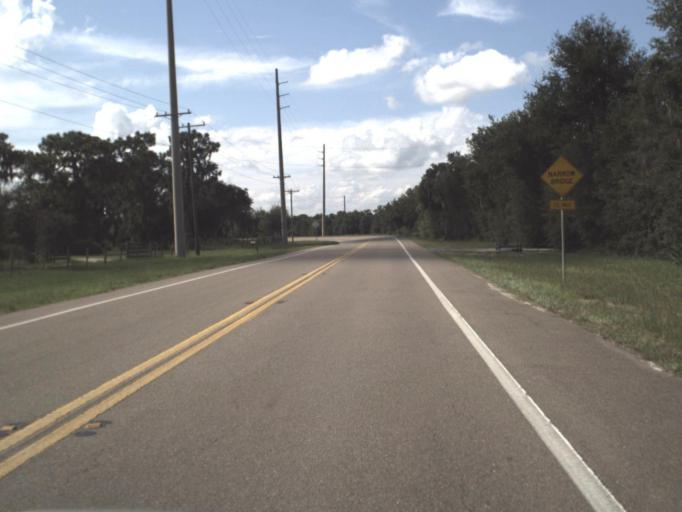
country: US
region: Florida
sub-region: Hardee County
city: Wauchula
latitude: 27.4864
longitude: -82.0151
